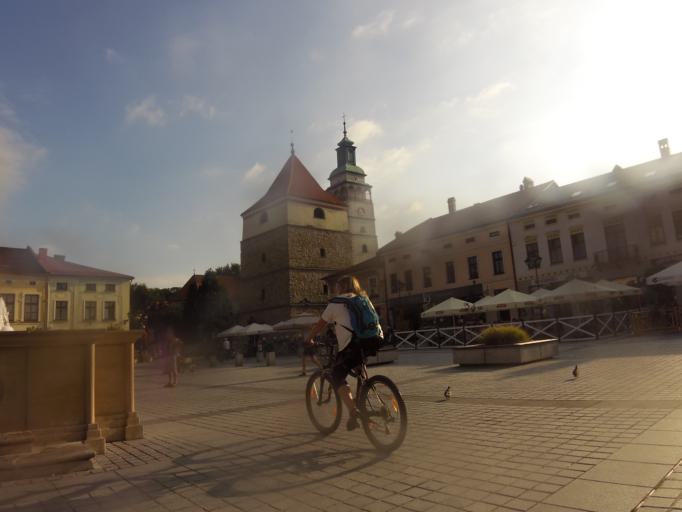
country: PL
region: Silesian Voivodeship
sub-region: Powiat zywiecki
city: Zywiec
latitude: 49.6892
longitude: 19.2030
